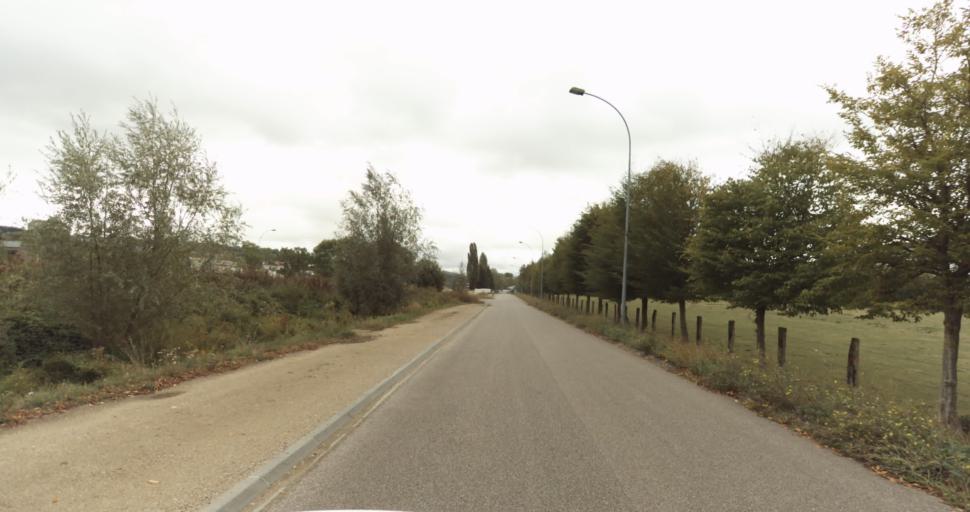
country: FR
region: Lower Normandy
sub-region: Departement de l'Orne
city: Vimoutiers
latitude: 48.9367
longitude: 0.1935
